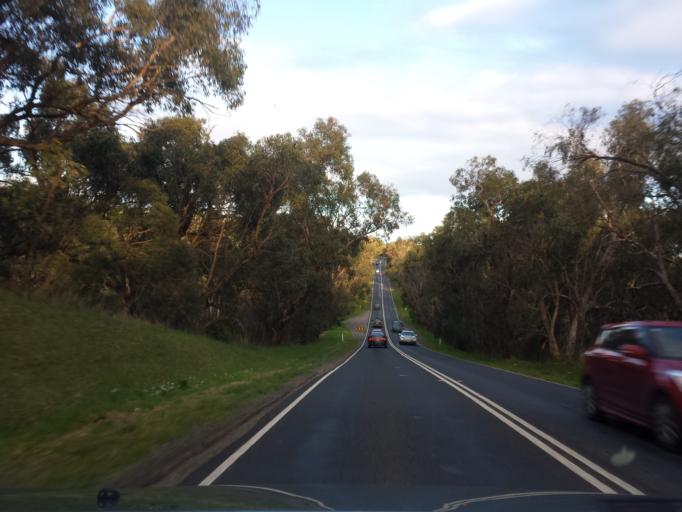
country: AU
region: Victoria
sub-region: Yarra Ranges
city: Lysterfield
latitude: -37.9379
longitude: 145.3129
